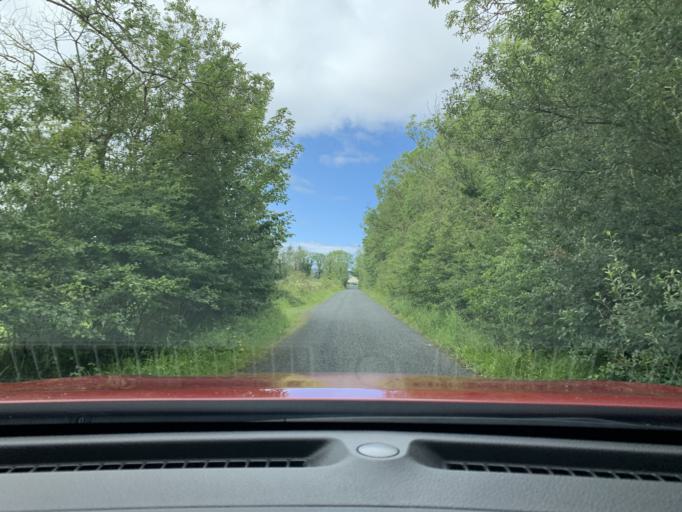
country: IE
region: Connaught
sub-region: Sligo
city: Sligo
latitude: 54.3313
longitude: -8.4968
